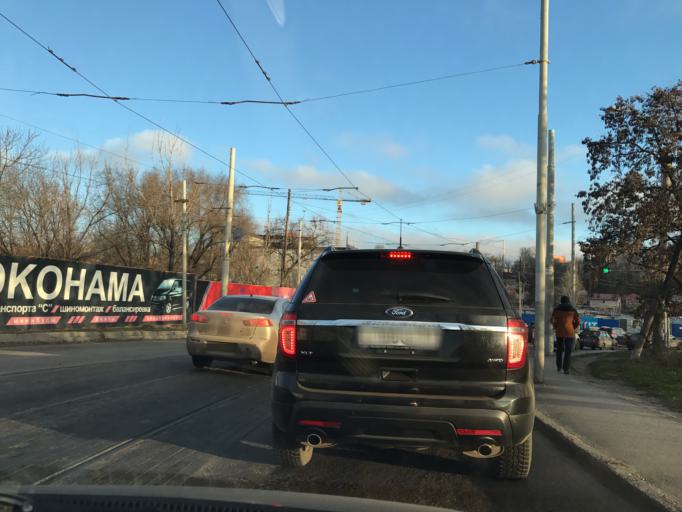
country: RU
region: Rostov
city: Rostov-na-Donu
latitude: 47.2237
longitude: 39.6858
